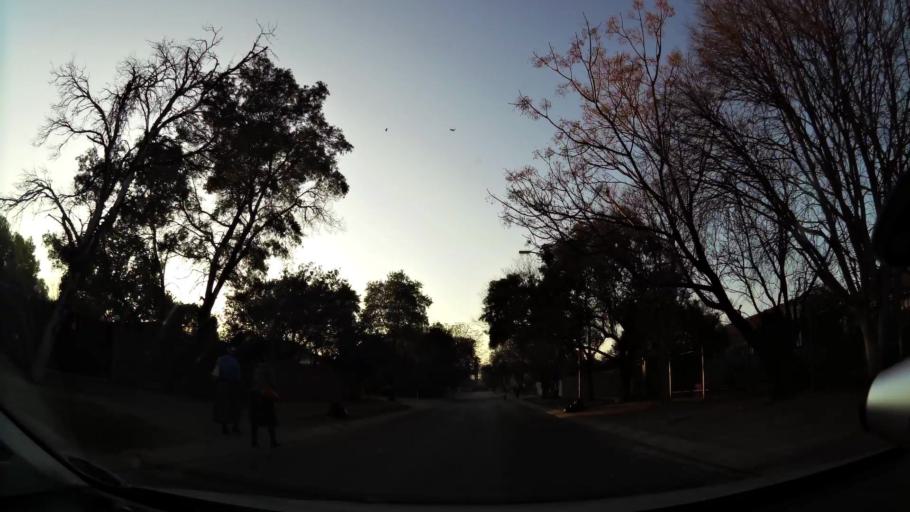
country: ZA
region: Orange Free State
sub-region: Mangaung Metropolitan Municipality
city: Bloemfontein
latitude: -29.1079
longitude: 26.1568
